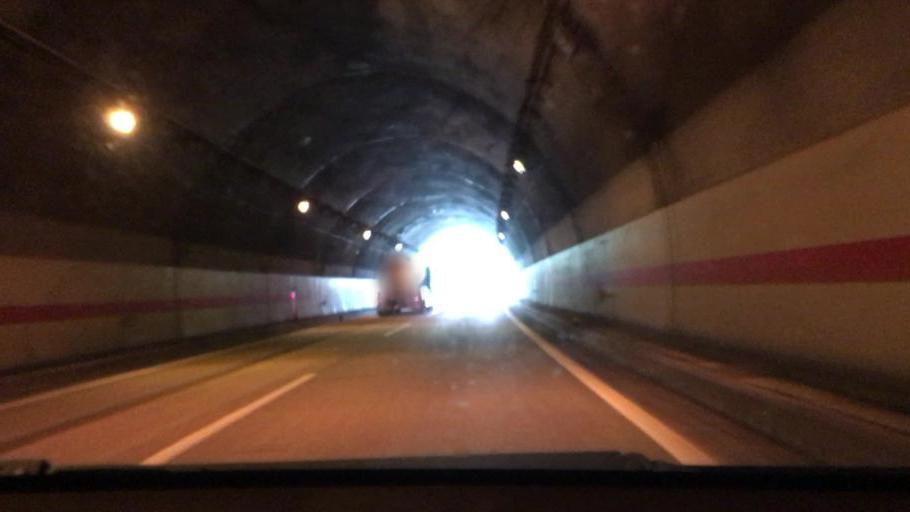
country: JP
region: Yamaguchi
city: Tokuyama
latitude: 34.0668
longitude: 131.6922
